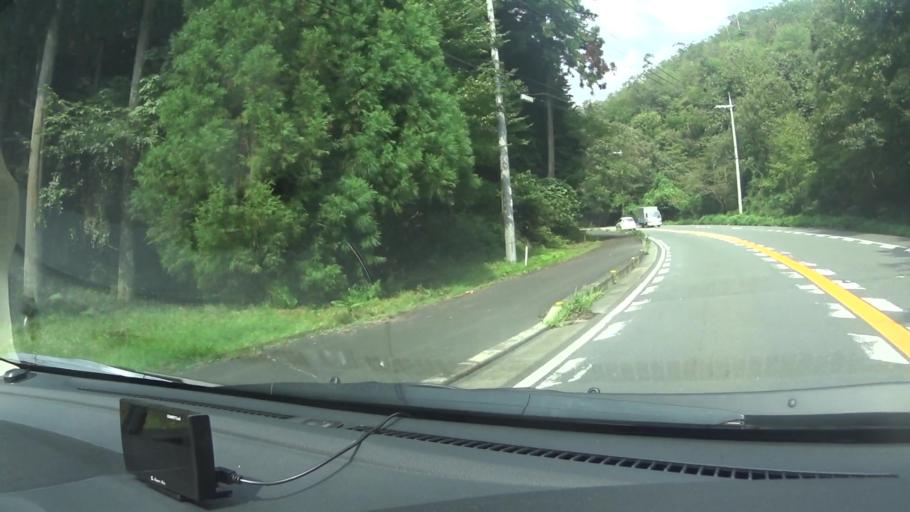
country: JP
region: Hyogo
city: Sasayama
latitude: 35.1653
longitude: 135.3581
